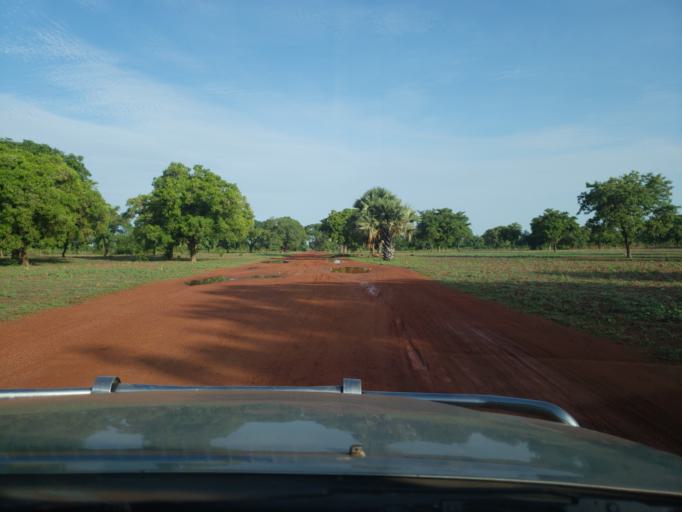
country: ML
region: Sikasso
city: Koutiala
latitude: 12.4250
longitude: -5.5940
